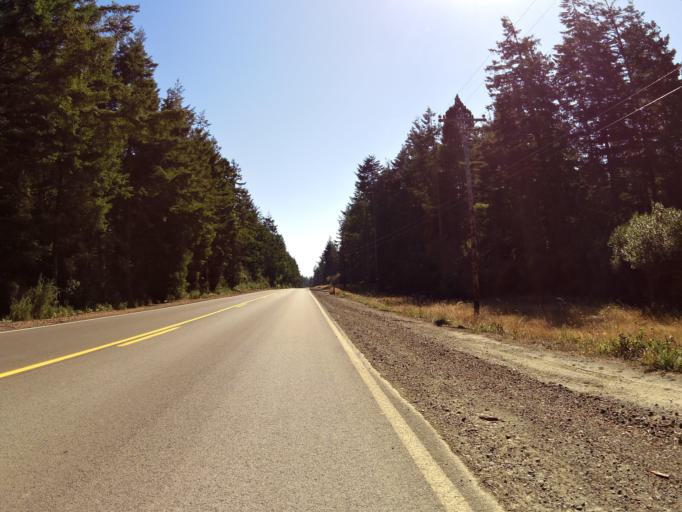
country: US
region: Oregon
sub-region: Coos County
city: Bandon
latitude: 43.2023
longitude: -124.3661
